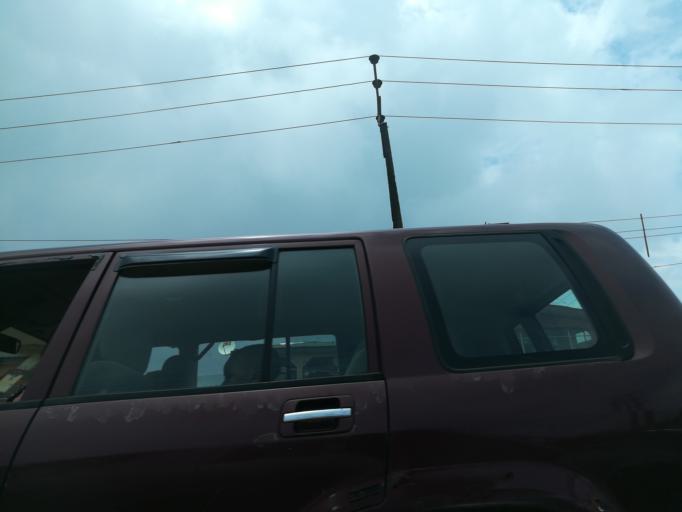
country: NG
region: Lagos
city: Ikorodu
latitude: 6.6611
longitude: 3.5195
